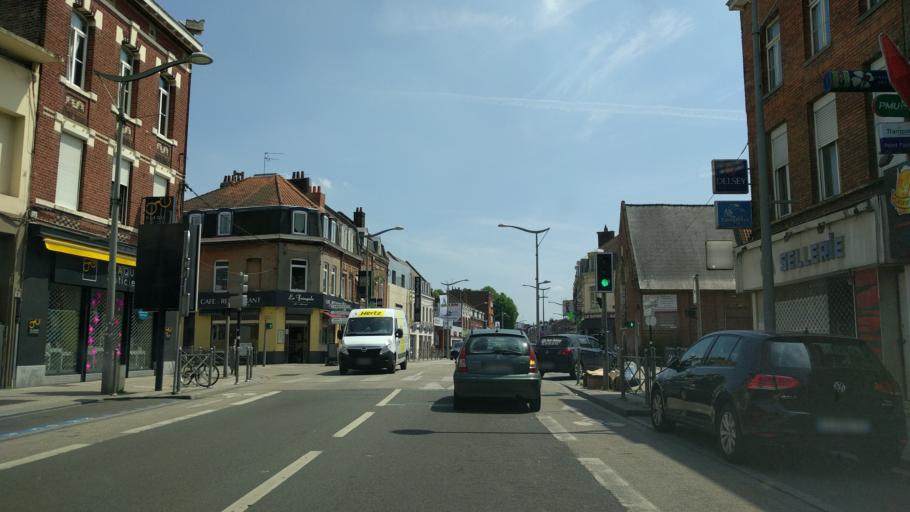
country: FR
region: Nord-Pas-de-Calais
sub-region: Departement du Nord
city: Lambersart
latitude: 50.6381
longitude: 3.0230
